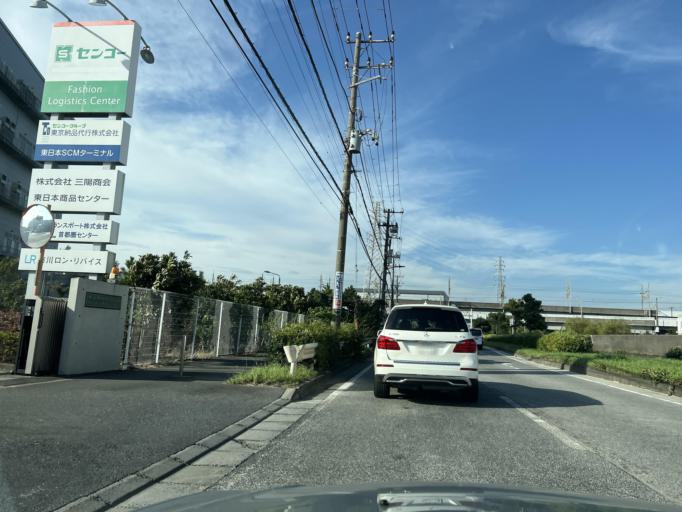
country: JP
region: Chiba
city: Funabashi
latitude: 35.6895
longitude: 139.9619
